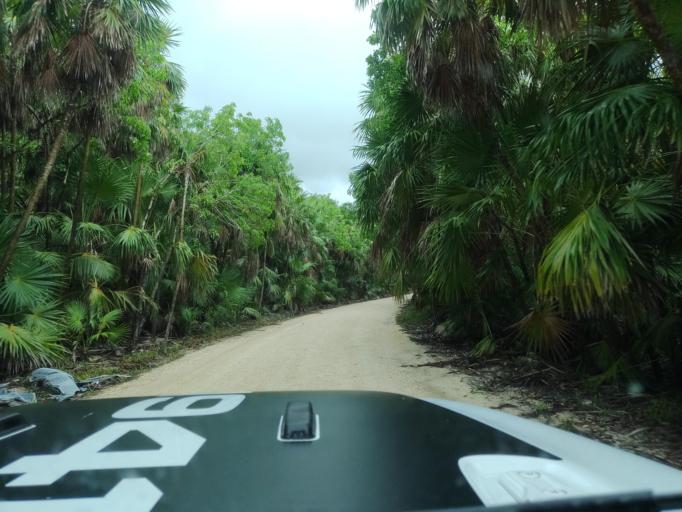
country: MX
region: Quintana Roo
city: Tulum
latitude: 20.0676
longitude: -87.4789
